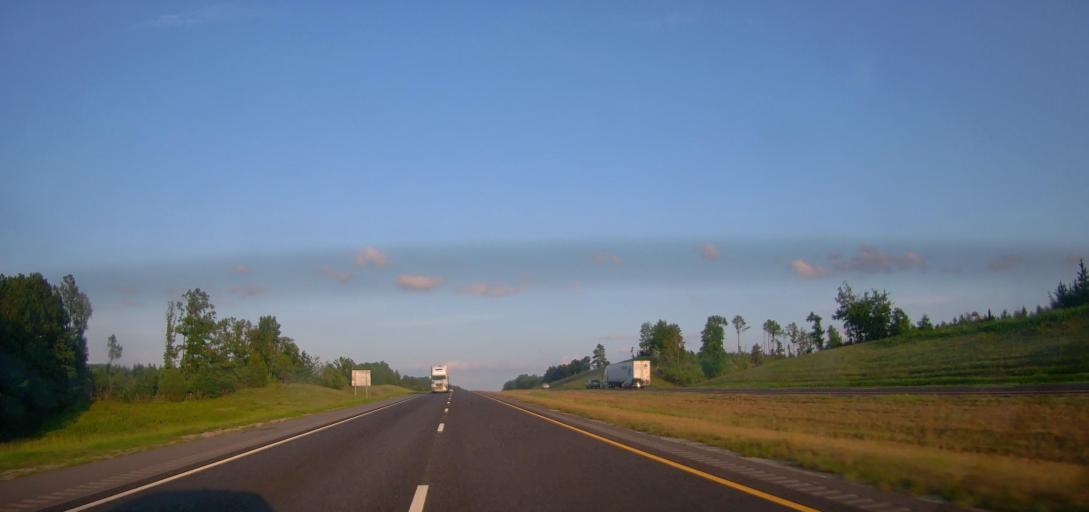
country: US
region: Alabama
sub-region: Marion County
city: Hamilton
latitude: 34.0660
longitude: -87.9578
